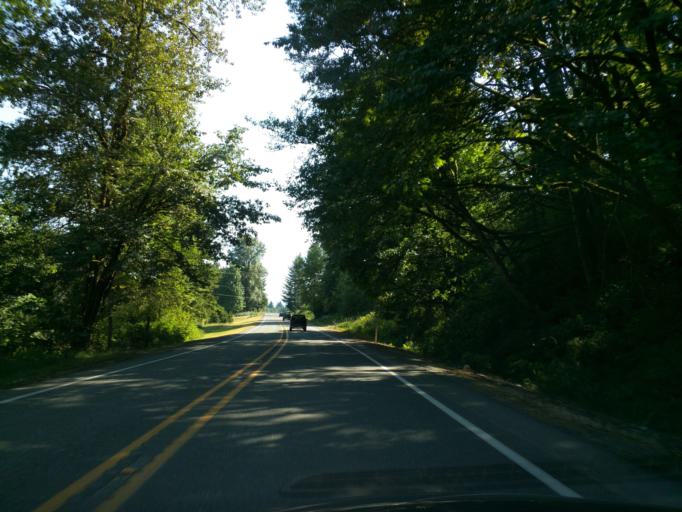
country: US
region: Washington
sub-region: Whatcom County
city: Peaceful Valley
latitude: 48.8472
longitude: -122.1627
